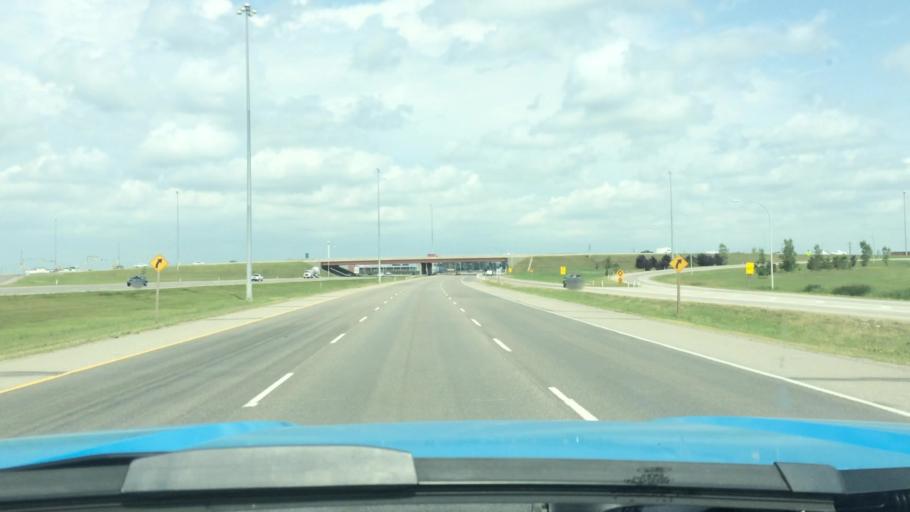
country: CA
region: Alberta
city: Airdrie
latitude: 51.2966
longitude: -114.0008
